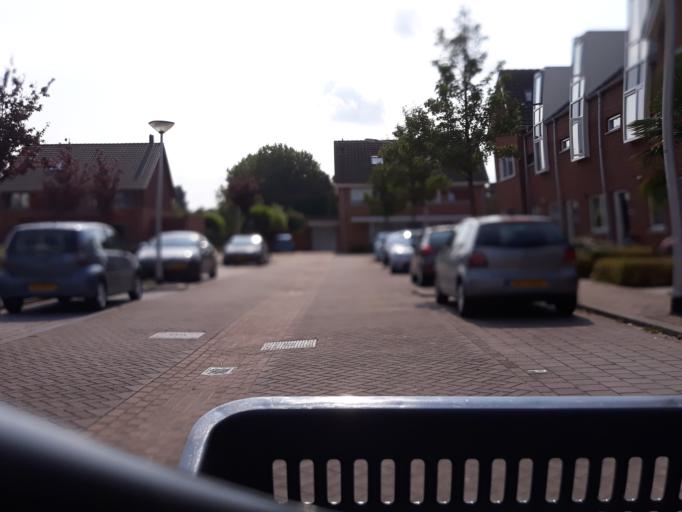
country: NL
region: South Holland
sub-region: Gemeente Hendrik-Ido-Ambacht
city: Hendrik-Ido-Ambacht
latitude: 51.8306
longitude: 4.6548
